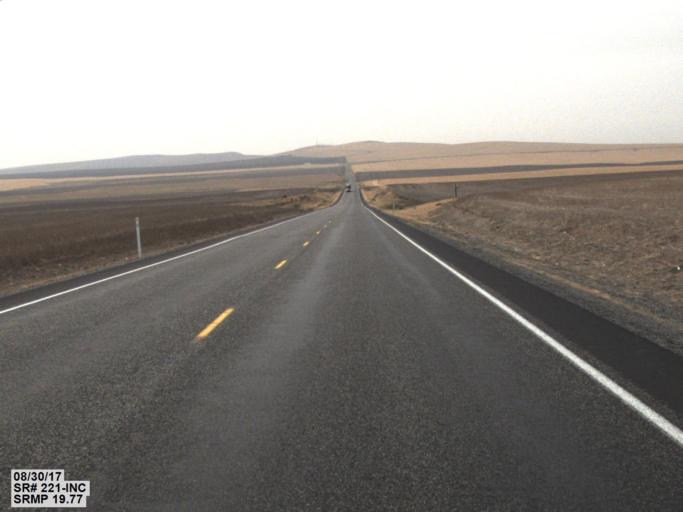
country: US
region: Washington
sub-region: Benton County
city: Prosser
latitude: 46.1871
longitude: -119.6530
